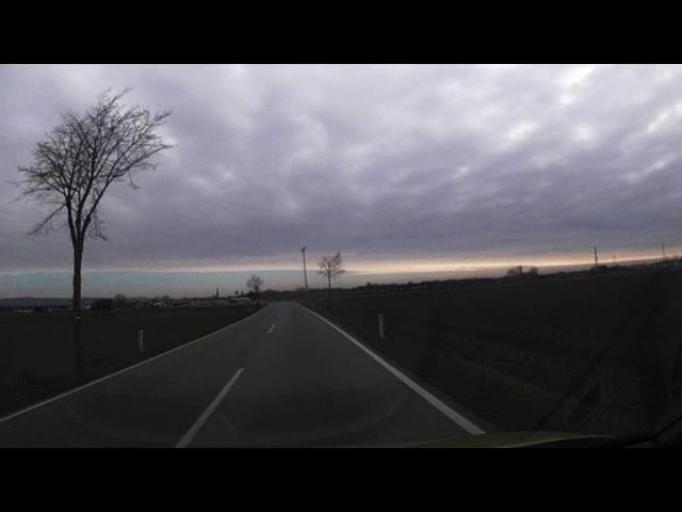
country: AT
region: Lower Austria
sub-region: Politischer Bezirk Wiener Neustadt
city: Ebenfurth
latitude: 47.8824
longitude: 16.3538
